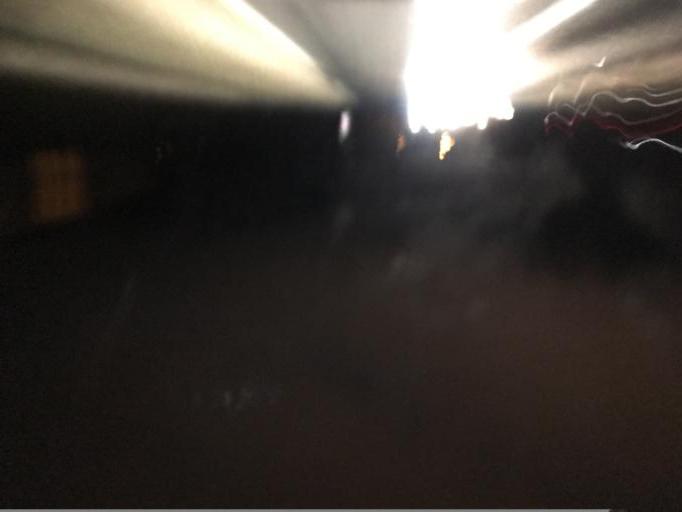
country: FR
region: Auvergne
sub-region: Departement de l'Allier
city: Hauterive
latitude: 46.0888
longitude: 3.4425
